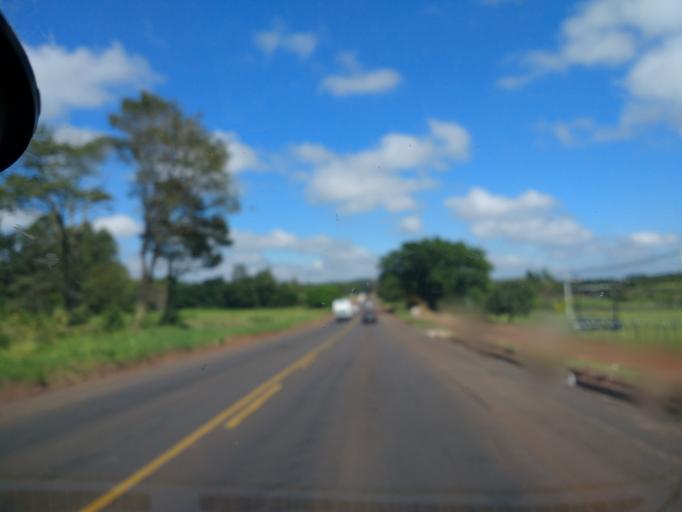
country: BR
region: Parana
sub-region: Cianorte
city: Cianorte
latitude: -23.7227
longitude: -52.6672
